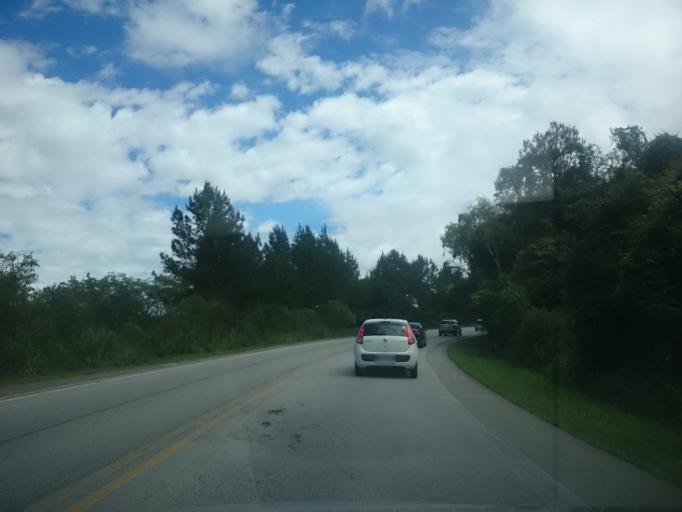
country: BR
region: Santa Catarina
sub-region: Anitapolis
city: Anitapolis
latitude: -27.6637
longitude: -49.1996
